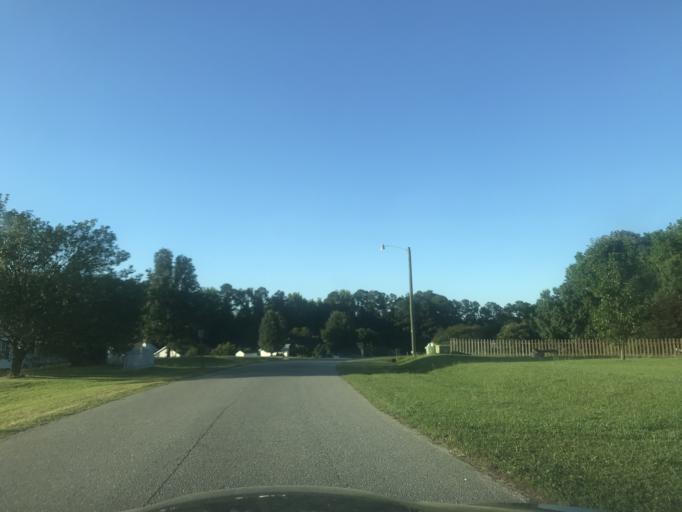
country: US
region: North Carolina
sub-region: Johnston County
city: Archer Lodge
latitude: 35.6803
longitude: -78.3609
